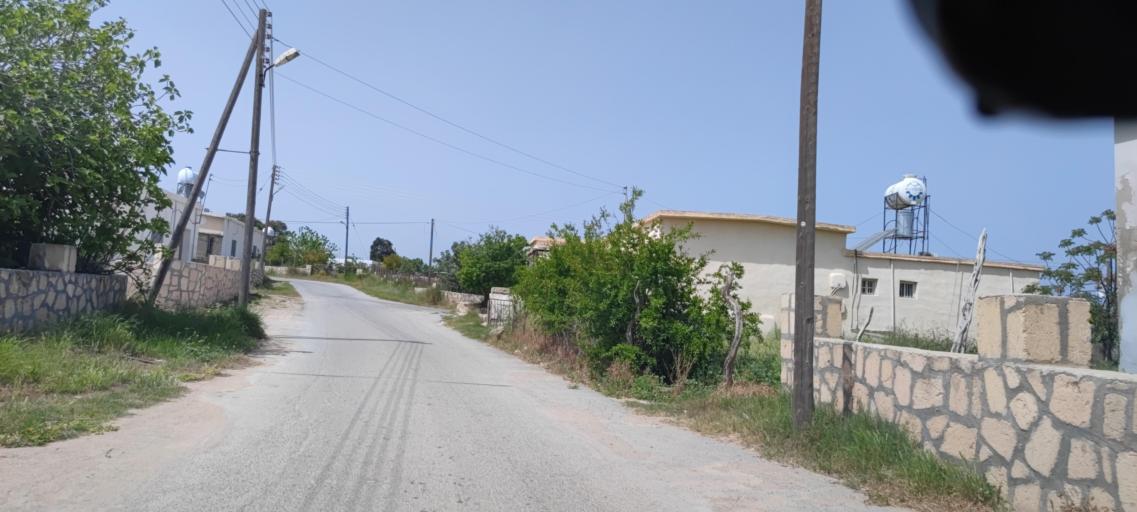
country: CY
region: Ammochostos
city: Rizokarpaso
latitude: 35.5923
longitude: 34.3809
